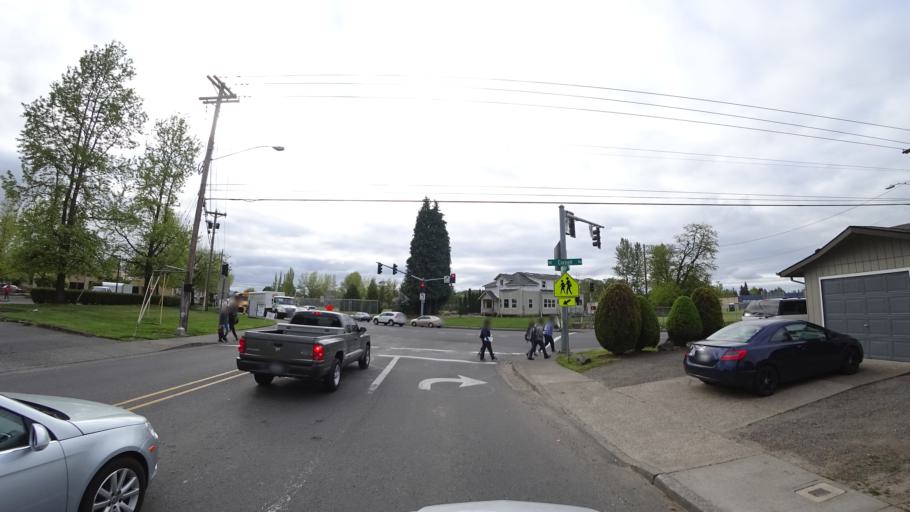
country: US
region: Oregon
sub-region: Washington County
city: Hillsboro
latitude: 45.5308
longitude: -122.9663
